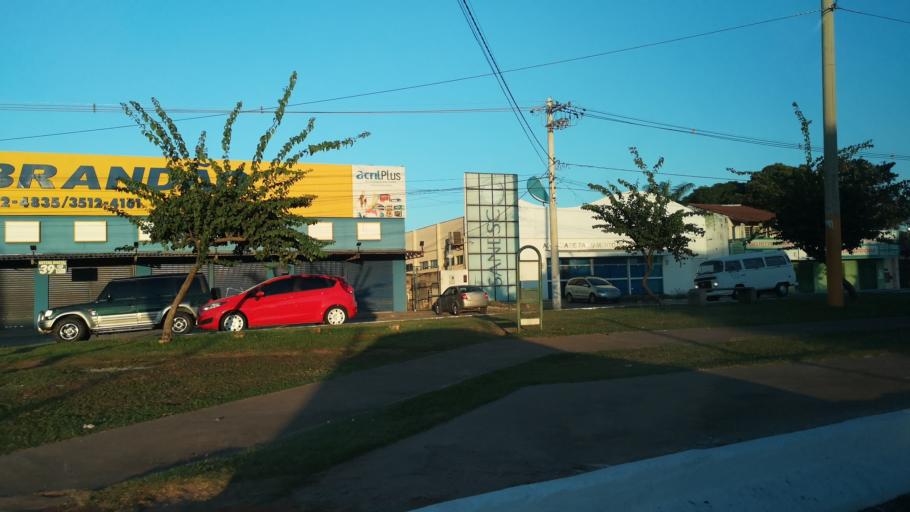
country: BR
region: Goias
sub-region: Senador Canedo
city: Senador Canedo
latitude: -16.6939
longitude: -49.1048
